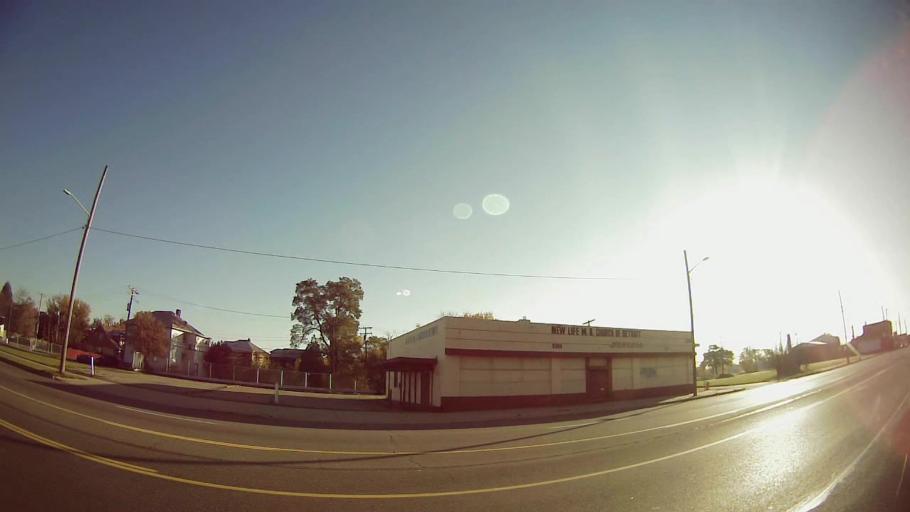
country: US
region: Michigan
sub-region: Wayne County
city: Hamtramck
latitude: 42.3894
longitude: -83.0225
